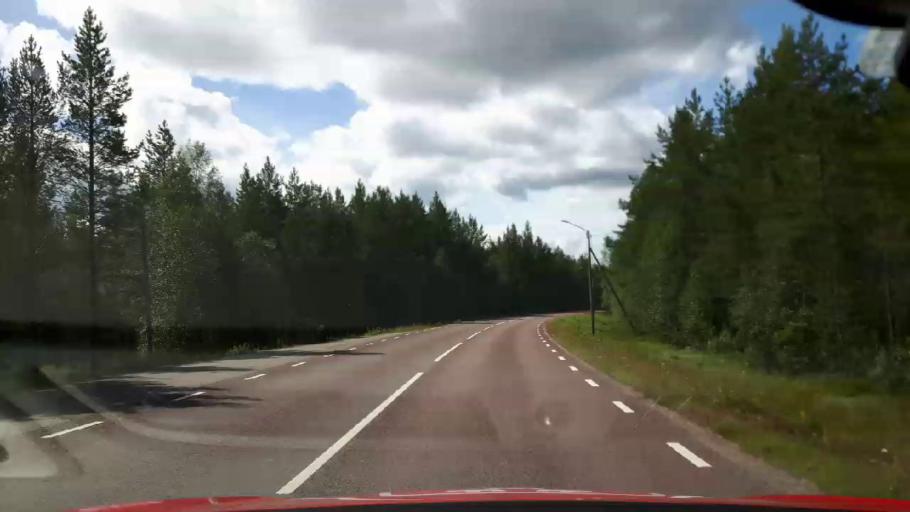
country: SE
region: Jaemtland
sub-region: Harjedalens Kommun
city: Sveg
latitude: 61.8617
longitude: 14.1090
